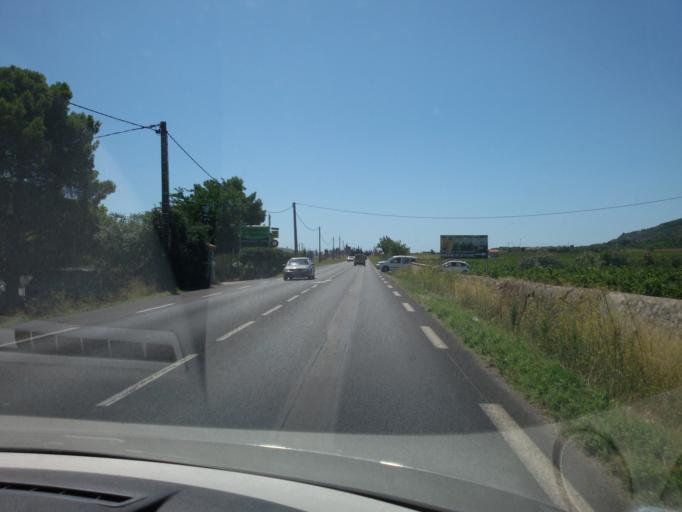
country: FR
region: Languedoc-Roussillon
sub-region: Departement de l'Herault
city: Vic-la-Gardiole
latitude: 43.4781
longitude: 3.7719
